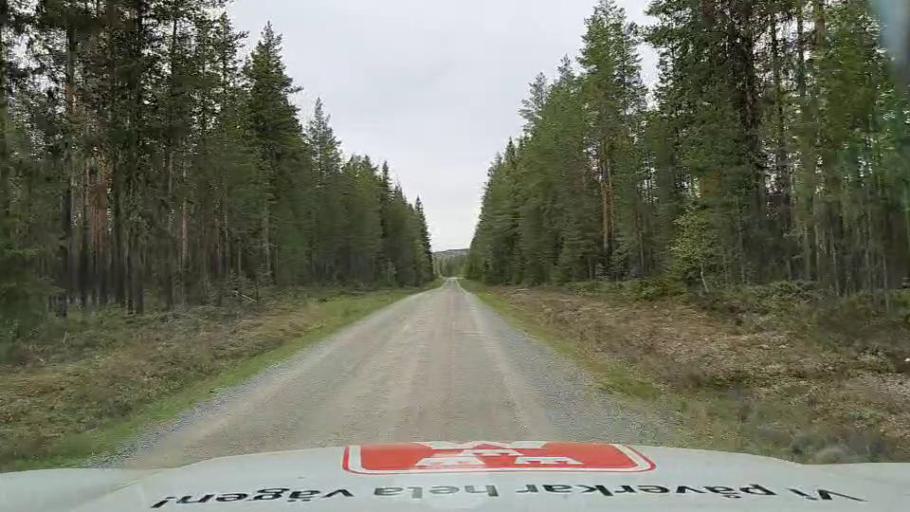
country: SE
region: Jaemtland
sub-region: Bergs Kommun
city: Hoverberg
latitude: 62.4997
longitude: 14.7060
